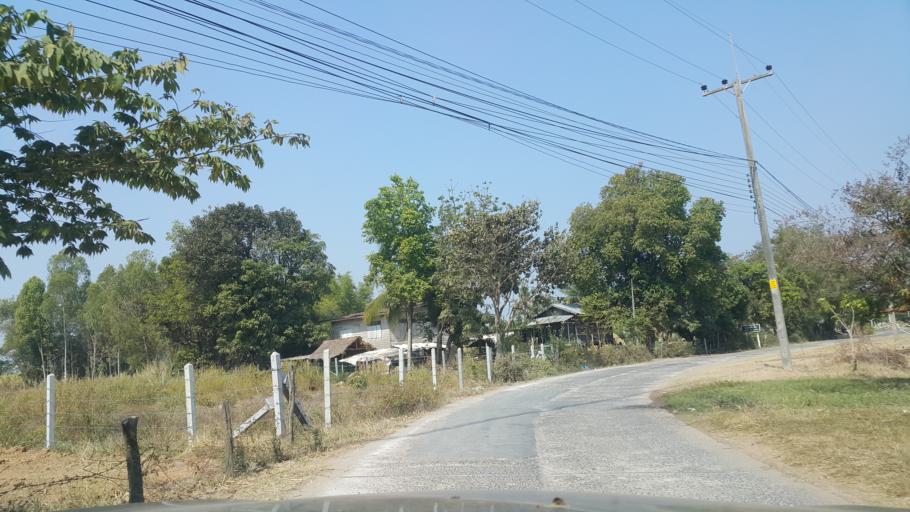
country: TH
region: Buriram
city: Satuek
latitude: 15.1359
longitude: 103.3453
